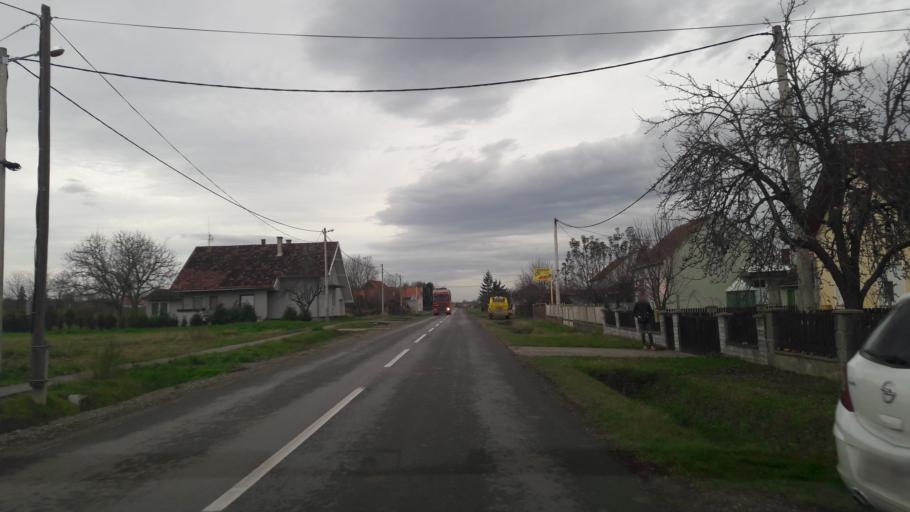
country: HR
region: Osjecko-Baranjska
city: Fericanci
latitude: 45.5310
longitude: 18.0280
